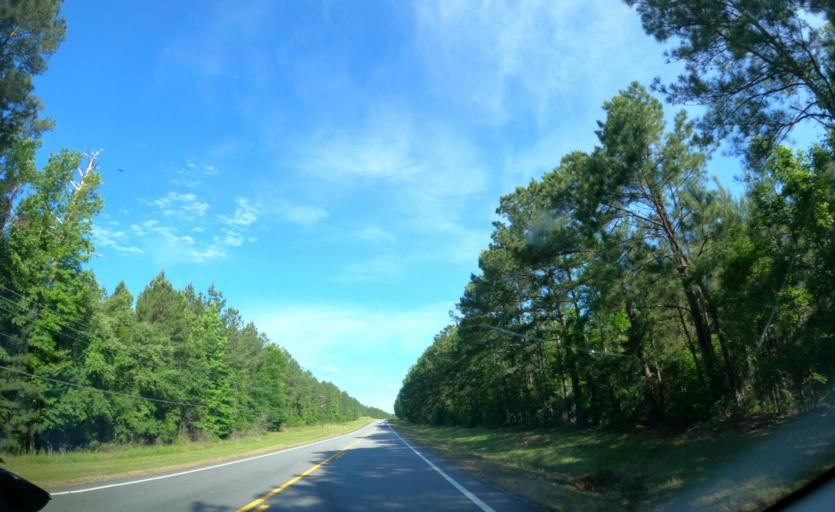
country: US
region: Georgia
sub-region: Columbia County
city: Appling
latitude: 33.6268
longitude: -82.2862
